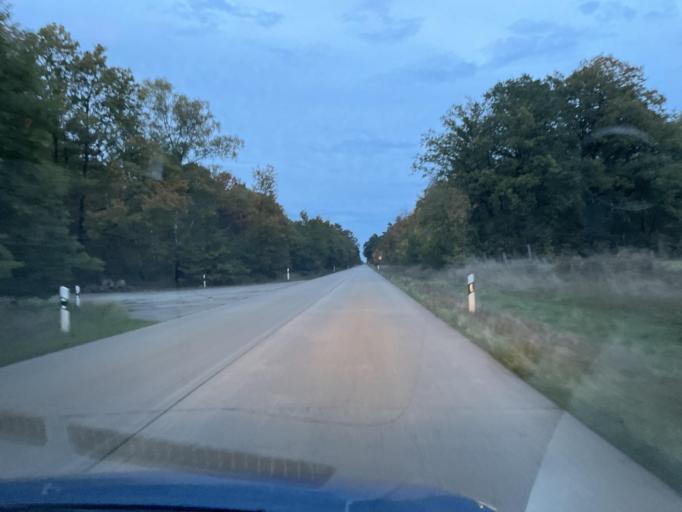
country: DE
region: Lower Saxony
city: Wriedel
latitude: 53.0047
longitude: 10.2237
